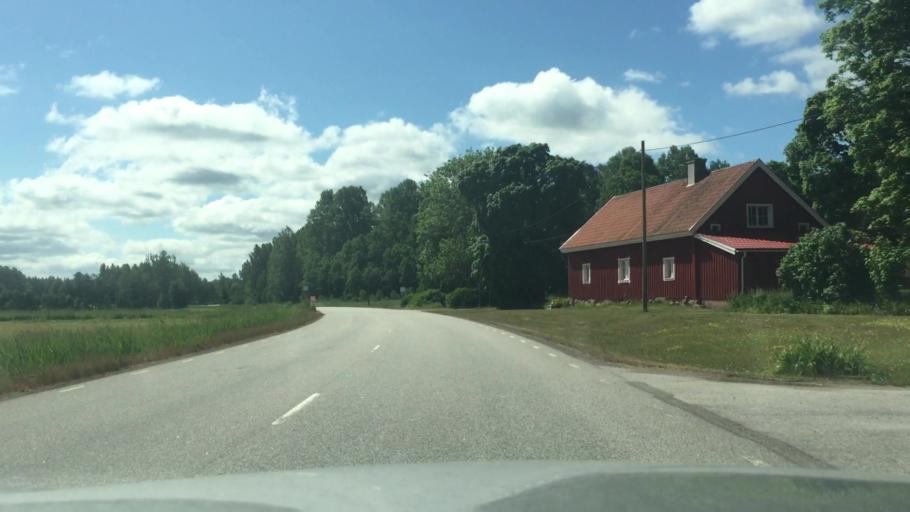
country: SE
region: Vaestra Goetaland
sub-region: Karlsborgs Kommun
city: Molltorp
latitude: 58.6300
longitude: 14.3884
